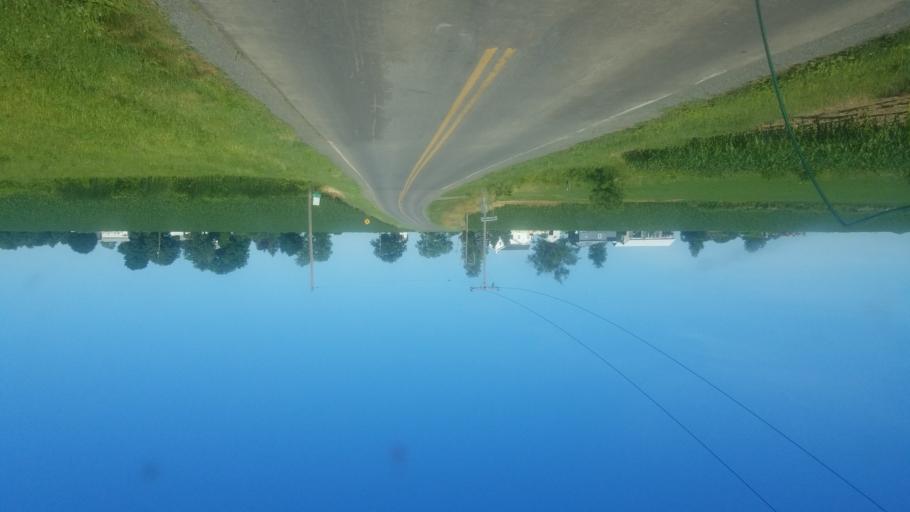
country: US
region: New York
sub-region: Ontario County
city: Clifton Springs
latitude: 42.8398
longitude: -77.1215
